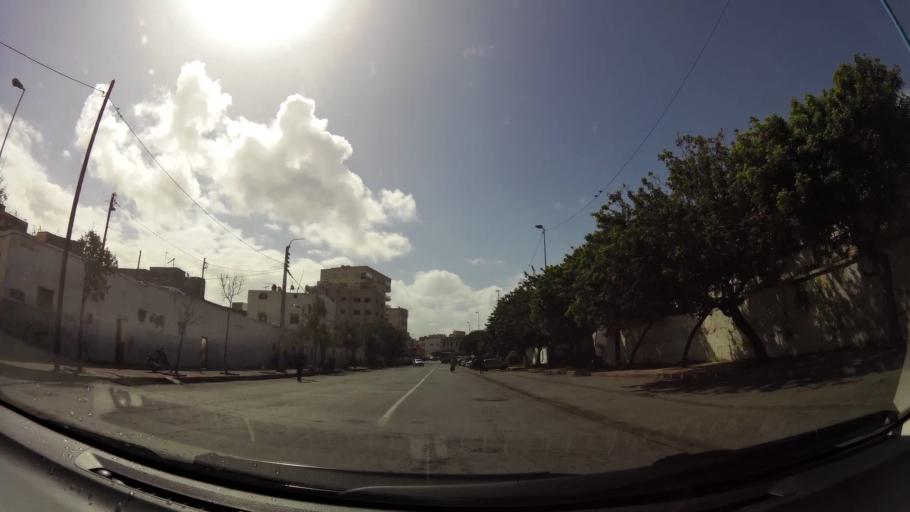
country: MA
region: Grand Casablanca
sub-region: Casablanca
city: Casablanca
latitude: 33.6050
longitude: -7.6287
